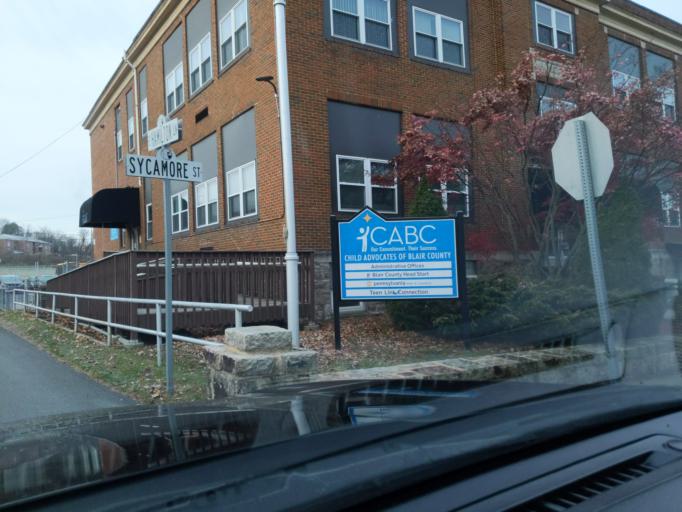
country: US
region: Pennsylvania
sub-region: Blair County
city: Greenwood
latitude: 40.5303
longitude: -78.3690
